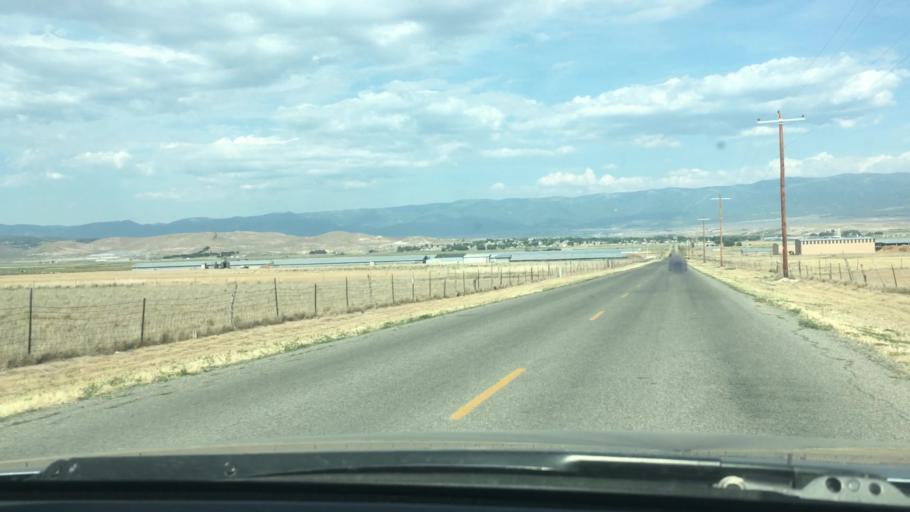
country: US
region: Utah
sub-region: Sanpete County
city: Moroni
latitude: 39.5235
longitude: -111.6359
